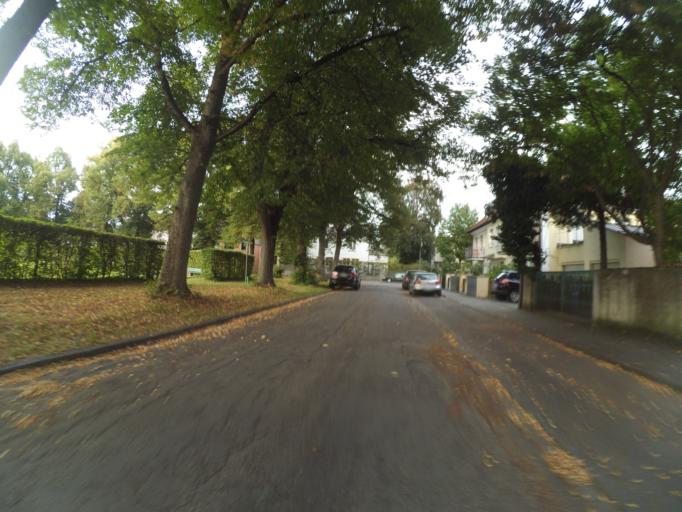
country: DE
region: Bavaria
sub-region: Upper Bavaria
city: Pasing
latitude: 48.1628
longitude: 11.5107
